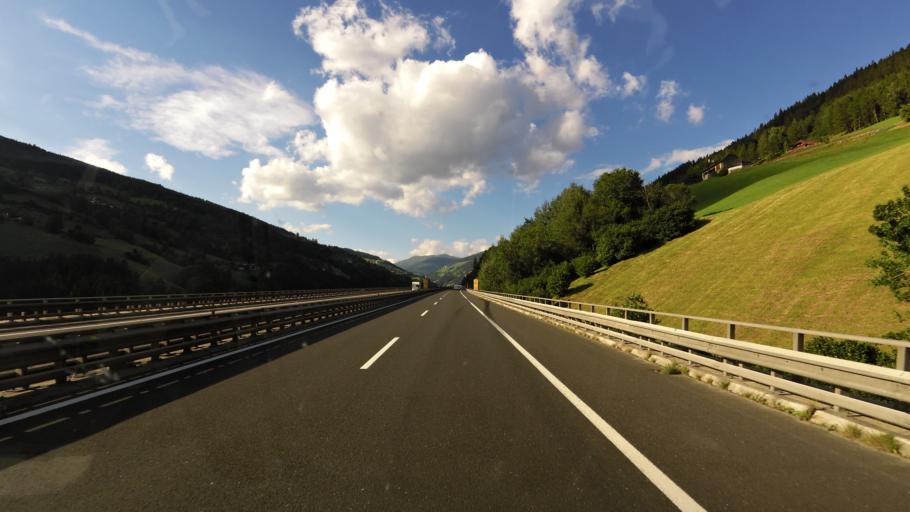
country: AT
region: Carinthia
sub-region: Politischer Bezirk Spittal an der Drau
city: Gmuend
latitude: 46.9440
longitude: 13.6101
